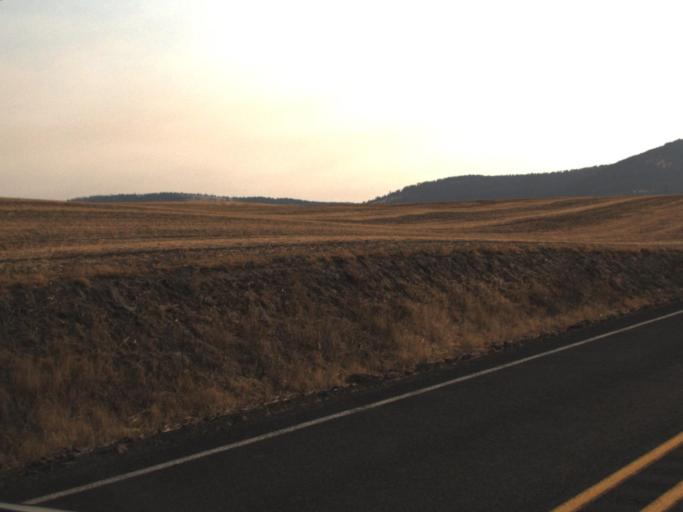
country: US
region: Idaho
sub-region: Benewah County
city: Plummer
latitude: 47.2754
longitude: -117.1453
